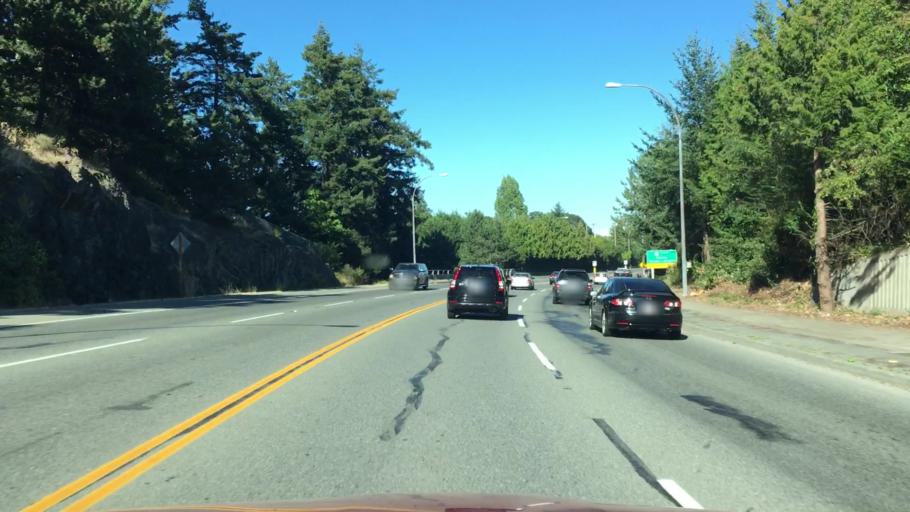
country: CA
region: British Columbia
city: Victoria
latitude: 48.4659
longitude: -123.3968
